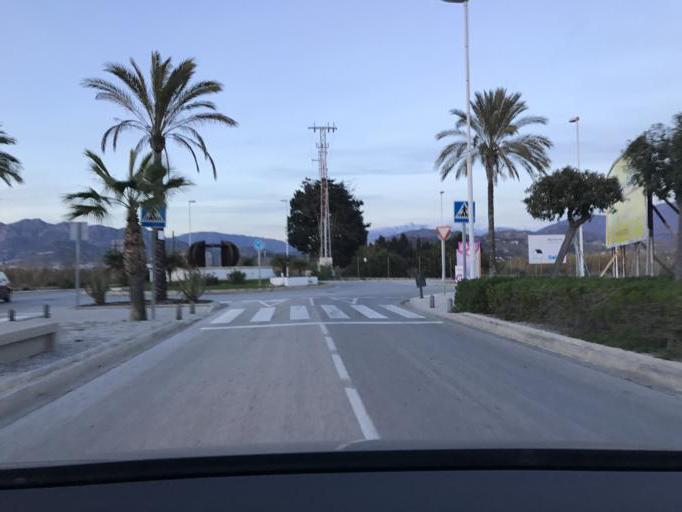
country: ES
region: Andalusia
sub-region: Provincia de Granada
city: Salobrena
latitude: 36.7232
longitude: -3.5593
